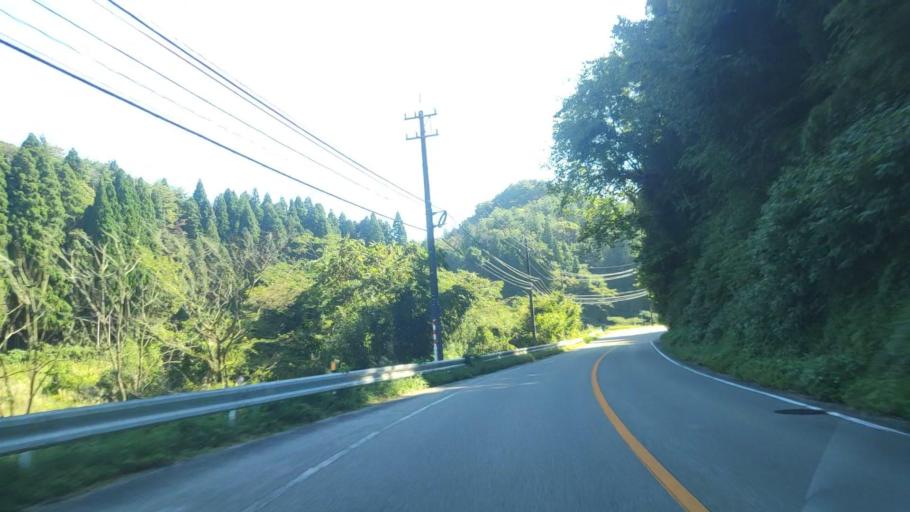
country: JP
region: Ishikawa
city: Nanao
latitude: 37.3306
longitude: 137.2088
